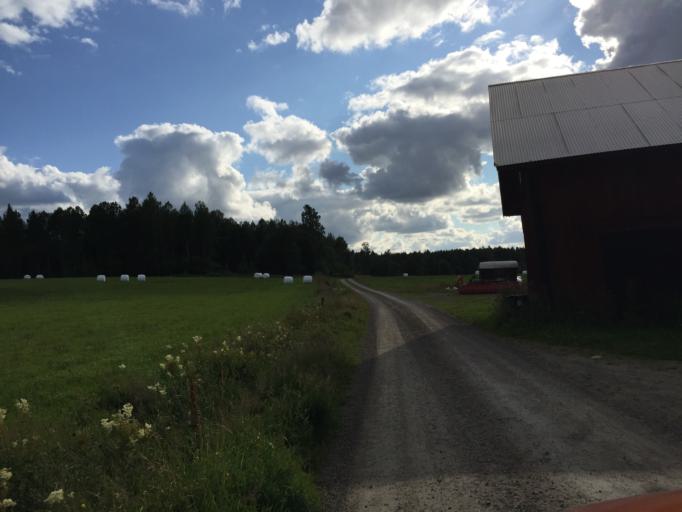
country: SE
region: Soedermanland
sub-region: Vingakers Kommun
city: Vingaker
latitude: 58.9839
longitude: 15.7112
